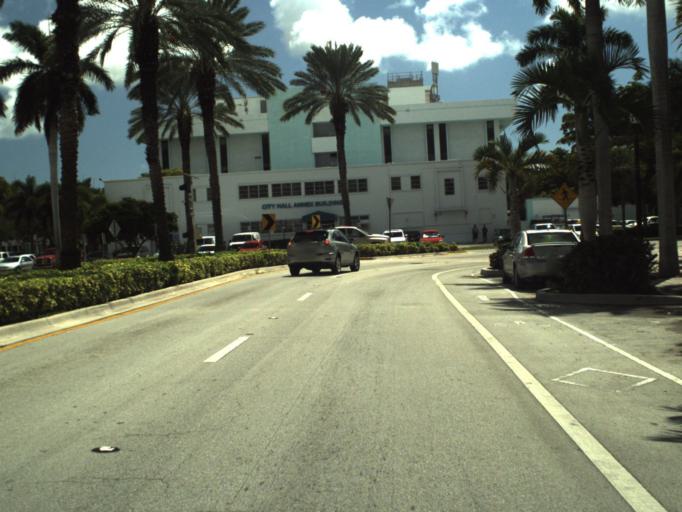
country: US
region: Florida
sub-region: Broward County
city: Hollywood
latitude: 26.0110
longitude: -80.1609
